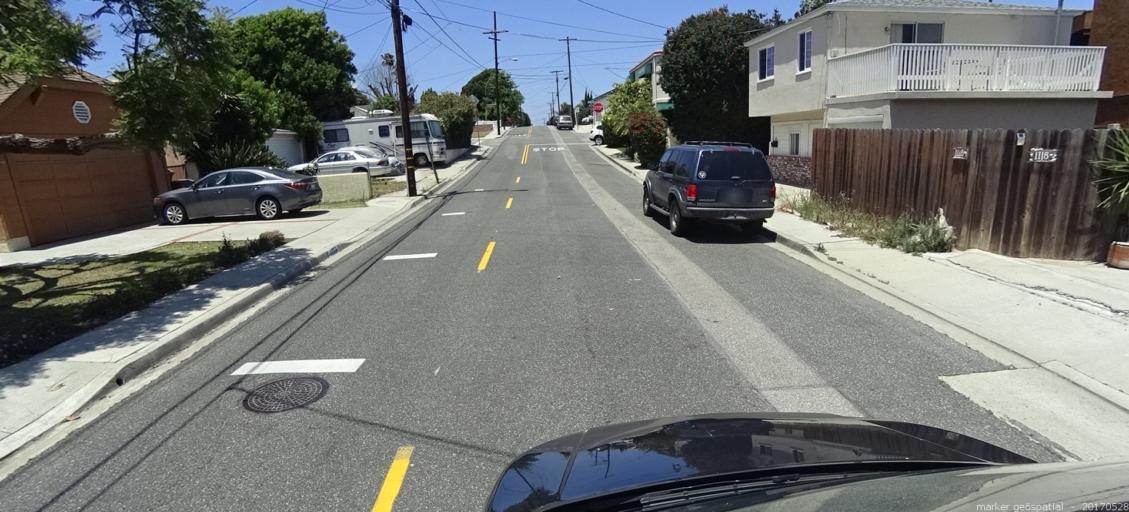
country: US
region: California
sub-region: Los Angeles County
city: Redondo Beach
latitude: 33.8647
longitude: -118.3825
